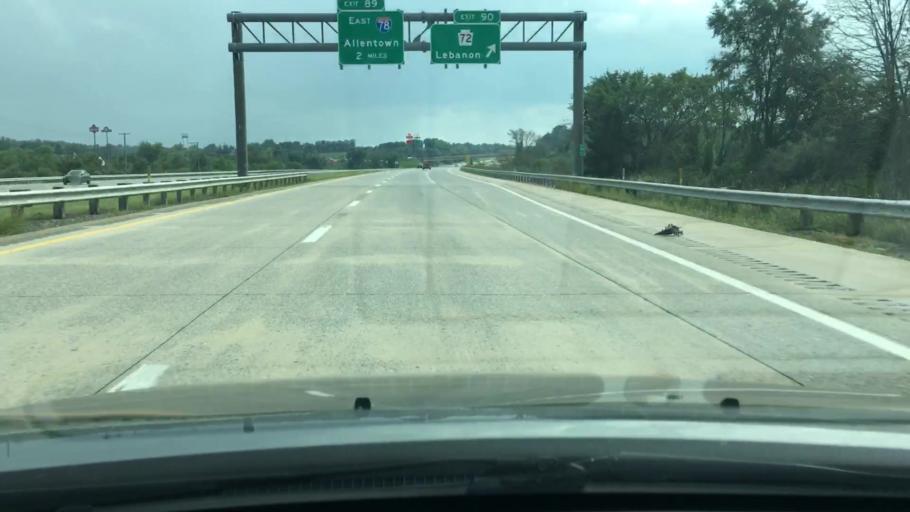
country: US
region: Pennsylvania
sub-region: Lebanon County
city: Jonestown
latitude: 40.4567
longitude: -76.5167
